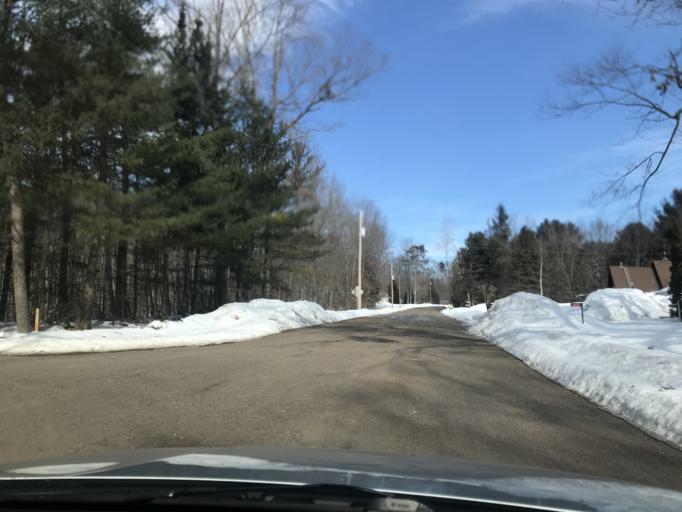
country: US
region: Wisconsin
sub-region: Oconto County
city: Gillett
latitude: 45.1196
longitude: -88.4188
